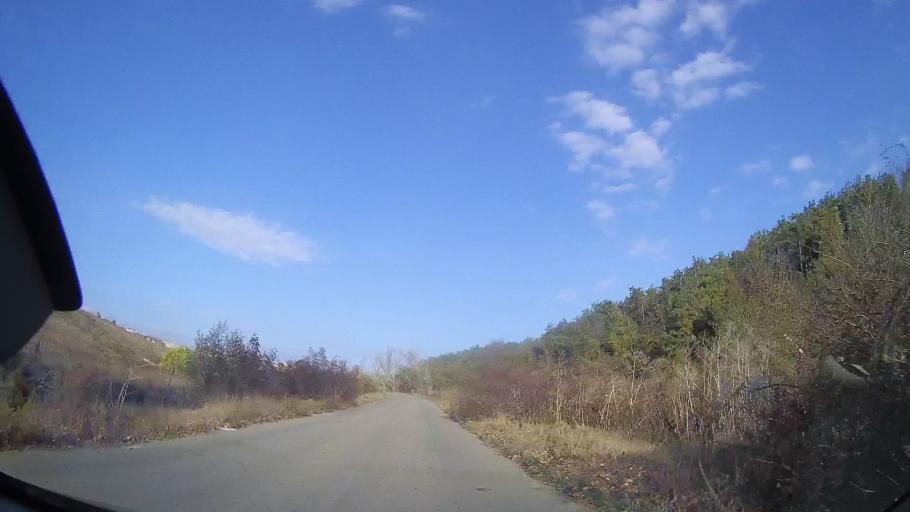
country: RO
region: Constanta
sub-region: Comuna Limanu
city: Limanu
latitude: 43.8194
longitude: 28.5192
